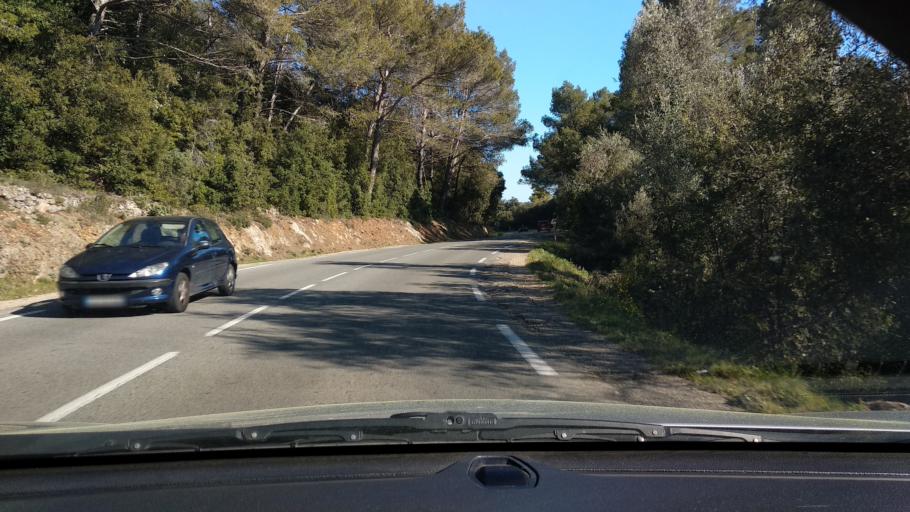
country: FR
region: Provence-Alpes-Cote d'Azur
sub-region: Departement des Alpes-Maritimes
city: Le Tignet
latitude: 43.6351
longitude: 6.8304
